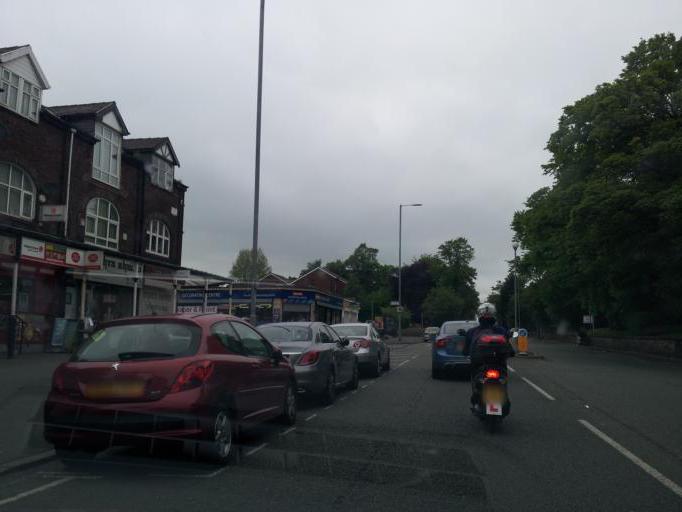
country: GB
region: England
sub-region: Manchester
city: Crumpsall
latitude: 53.5190
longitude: -2.2488
